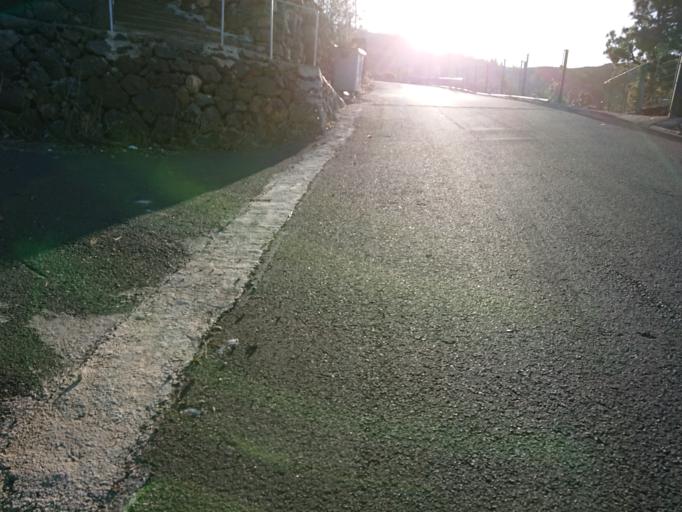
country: ES
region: Canary Islands
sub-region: Provincia de Santa Cruz de Tenerife
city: Tijarafe
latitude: 28.6800
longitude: -17.9411
